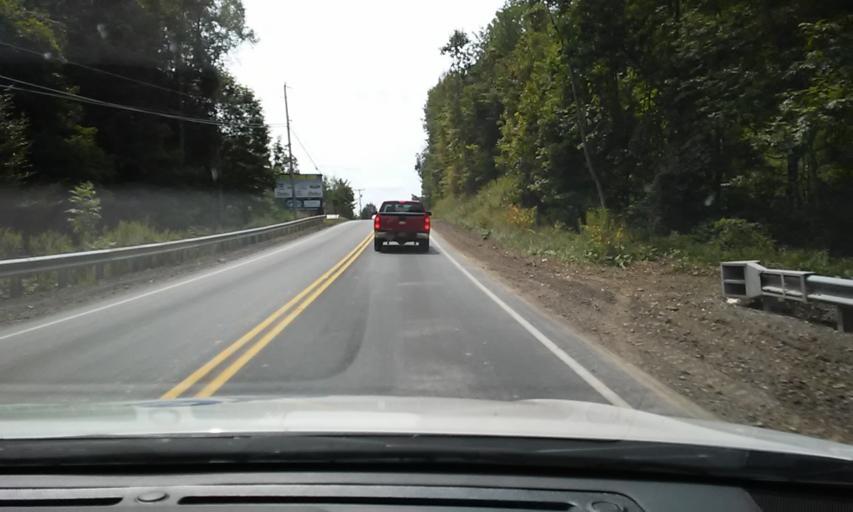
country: US
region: Pennsylvania
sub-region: Clearfield County
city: Treasure Lake
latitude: 41.1737
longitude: -78.6505
